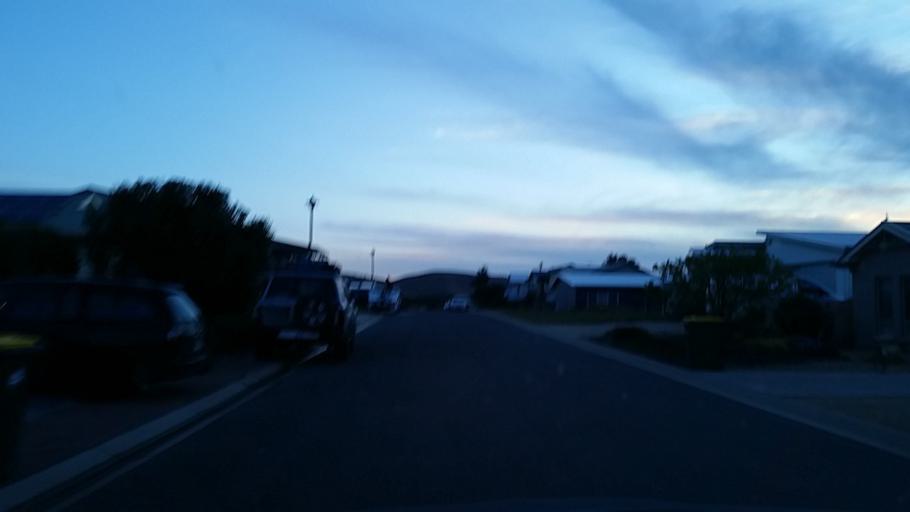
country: AU
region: South Australia
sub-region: Yankalilla
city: Normanville
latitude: -35.4511
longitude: 138.3167
